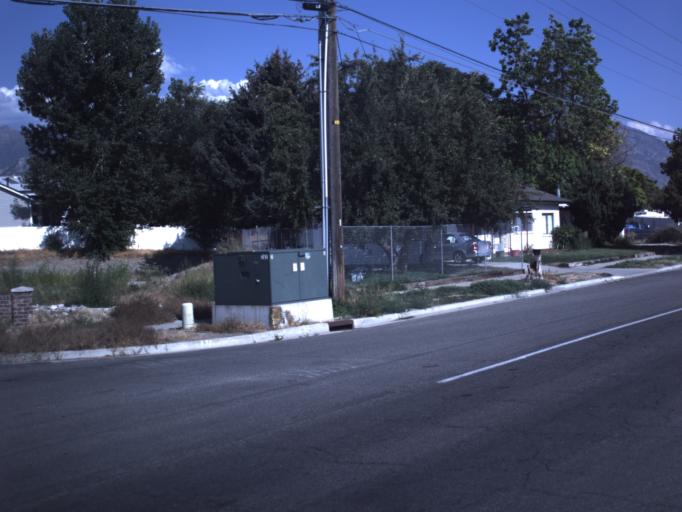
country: US
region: Utah
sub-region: Utah County
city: Orem
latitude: 40.2538
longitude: -111.7076
